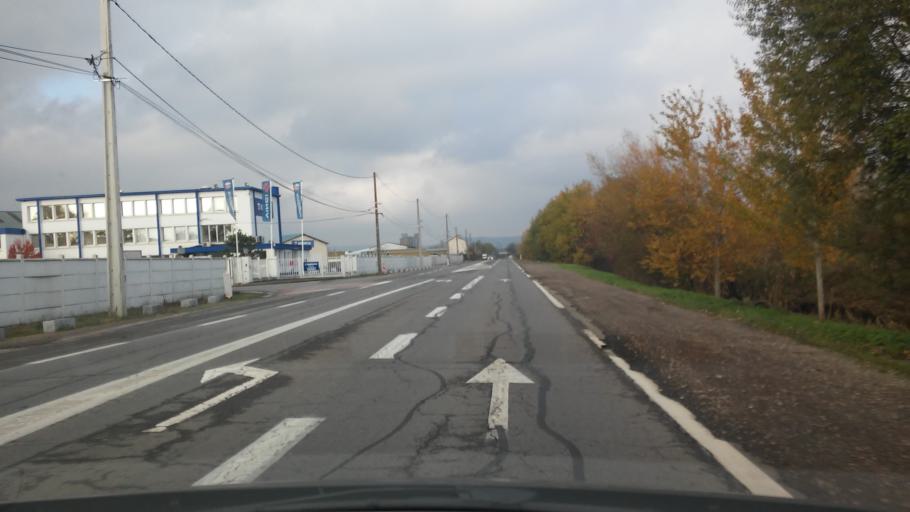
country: FR
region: Lorraine
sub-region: Departement de la Moselle
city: Uckange
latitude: 49.3182
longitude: 6.1561
